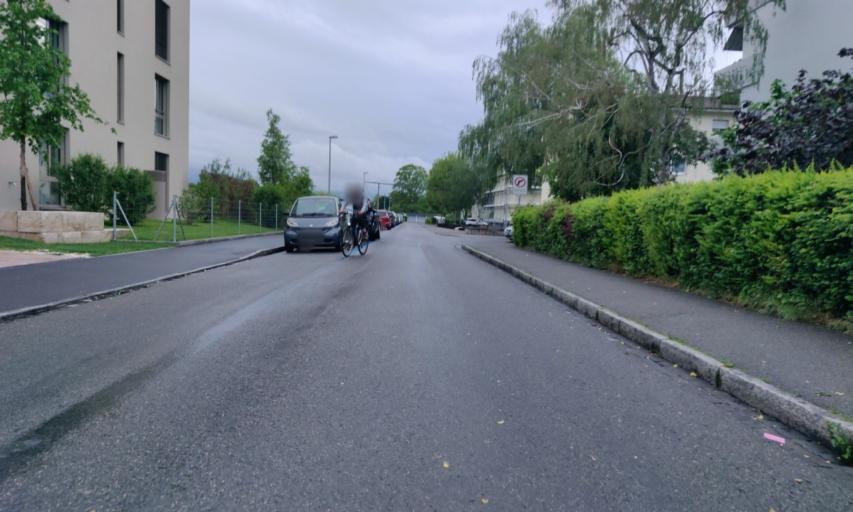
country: CH
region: Basel-City
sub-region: Basel-Stadt
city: Riehen
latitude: 47.5699
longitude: 7.6327
